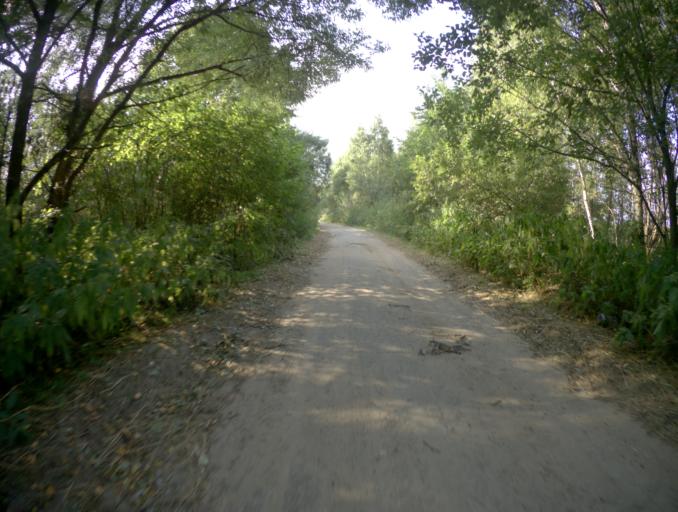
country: RU
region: Vladimir
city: Raduzhnyy
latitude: 56.0038
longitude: 40.3677
